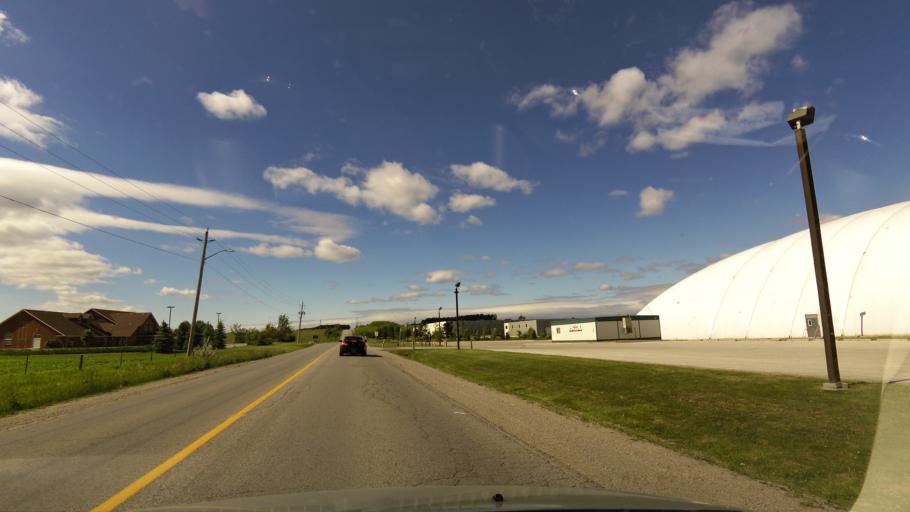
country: CA
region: Ontario
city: Bradford West Gwillimbury
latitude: 44.1157
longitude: -79.6045
